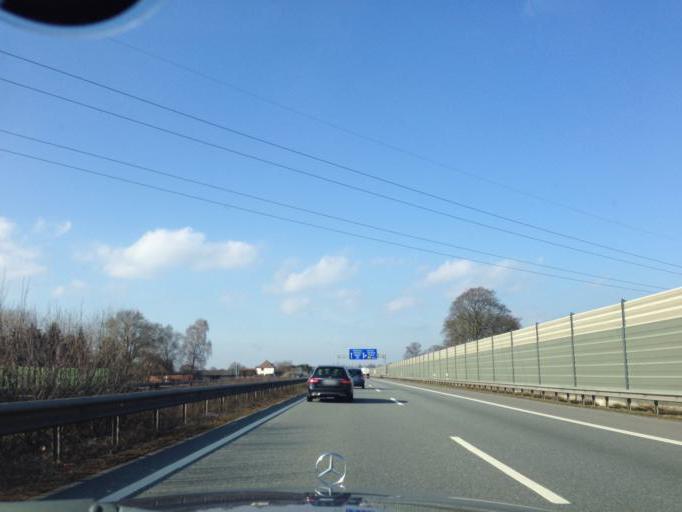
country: DE
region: Lower Saxony
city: Delmenhorst
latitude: 53.0229
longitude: 8.6861
